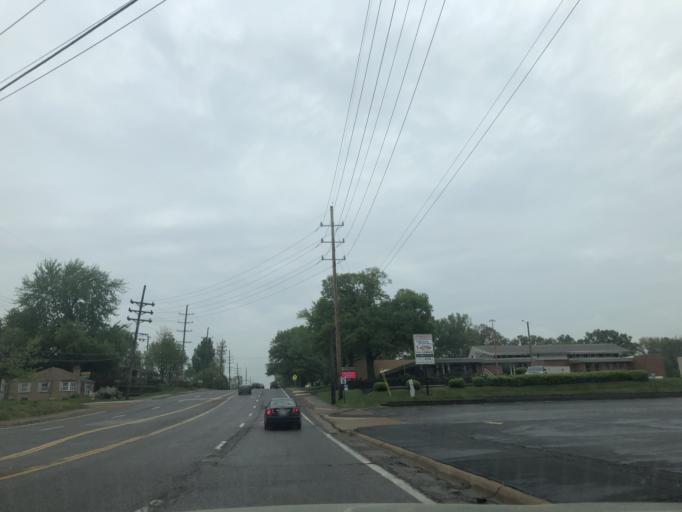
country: US
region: Missouri
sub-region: Saint Louis County
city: Marlborough
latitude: 38.5659
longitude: -90.3207
